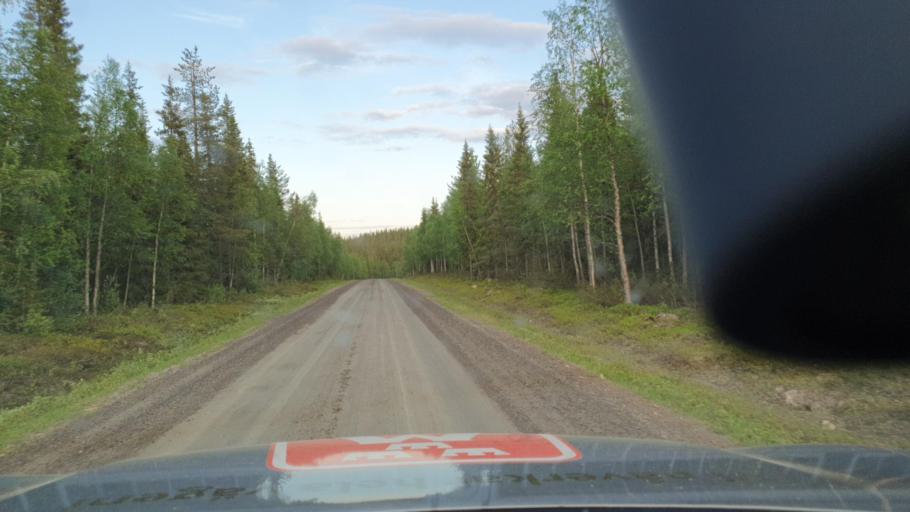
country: SE
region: Norrbotten
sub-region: Bodens Kommun
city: Boden
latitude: 66.5184
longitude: 21.5152
